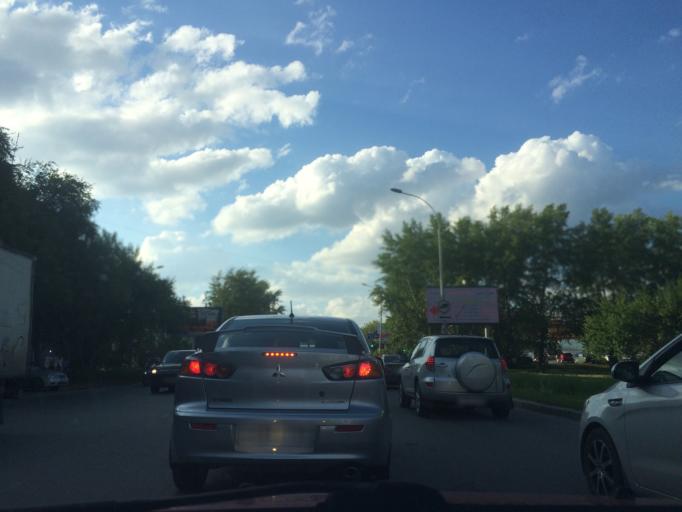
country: RU
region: Sverdlovsk
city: Yekaterinburg
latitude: 56.8204
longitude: 60.6399
